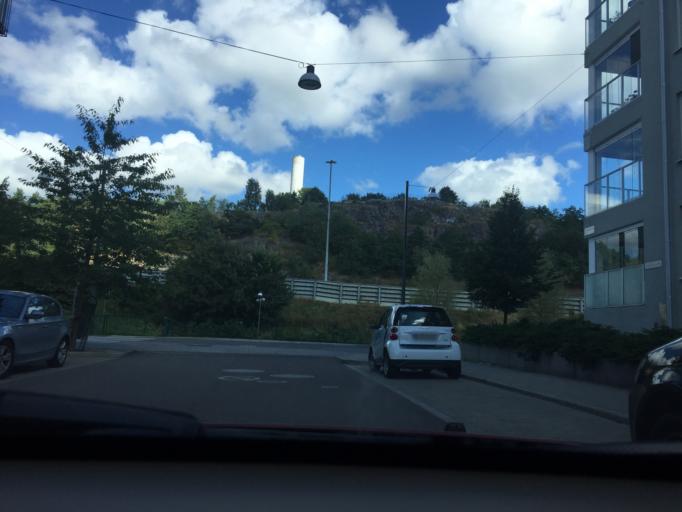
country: SE
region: Stockholm
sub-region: Stockholms Kommun
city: OEstermalm
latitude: 59.3072
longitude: 18.1096
